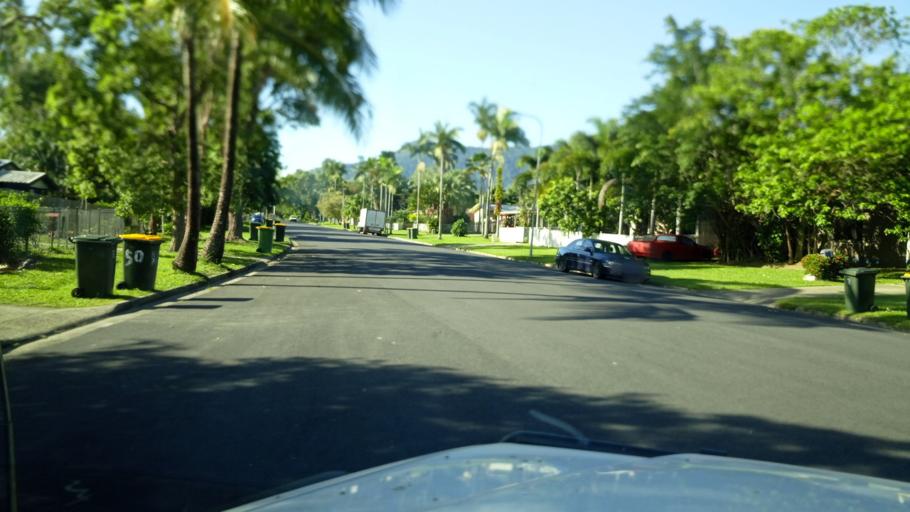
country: AU
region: Queensland
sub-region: Cairns
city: Woree
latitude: -16.9381
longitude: 145.7366
